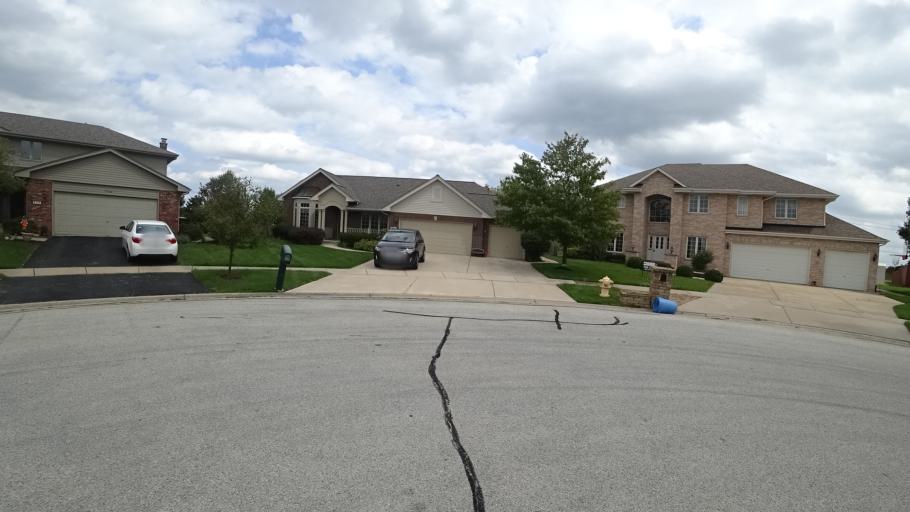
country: US
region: Illinois
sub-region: Cook County
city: Orland Hills
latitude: 41.5631
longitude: -87.8229
